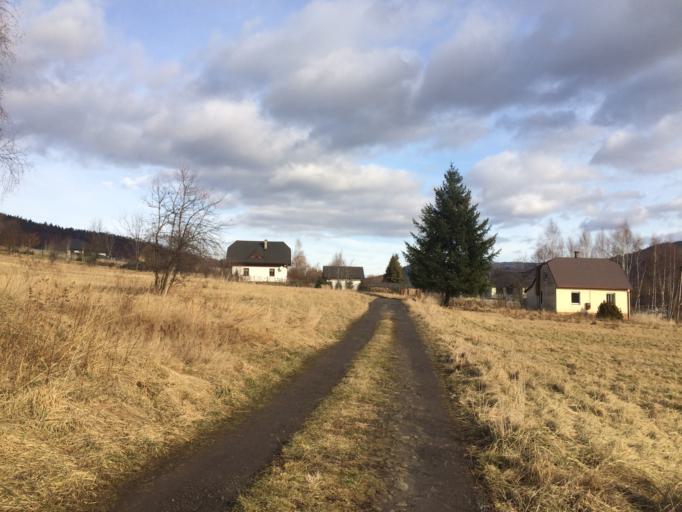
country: PL
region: Silesian Voivodeship
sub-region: Powiat bielski
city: Bystra
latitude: 49.7544
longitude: 19.0656
